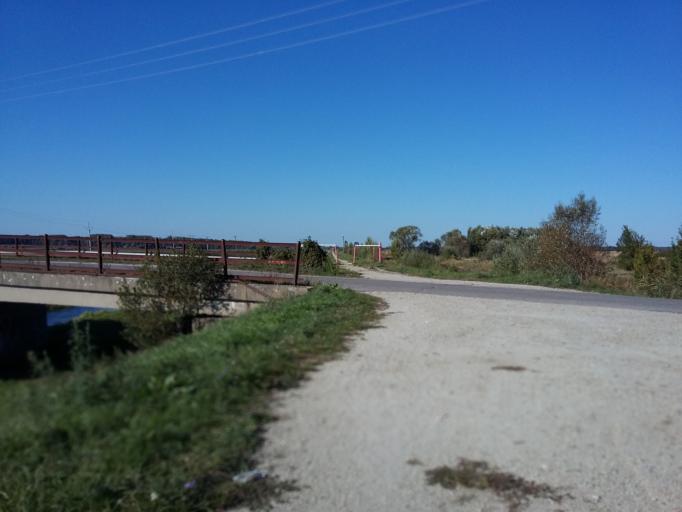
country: AT
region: Lower Austria
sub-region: Politischer Bezirk Ganserndorf
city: Marchegg
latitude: 48.3161
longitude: 16.9712
